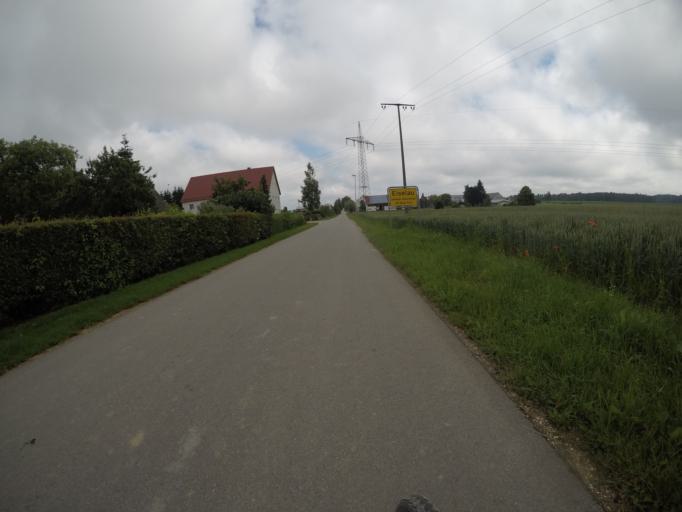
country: DE
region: Baden-Wuerttemberg
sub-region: Tuebingen Region
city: Dornstadt
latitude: 48.4908
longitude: 9.9521
